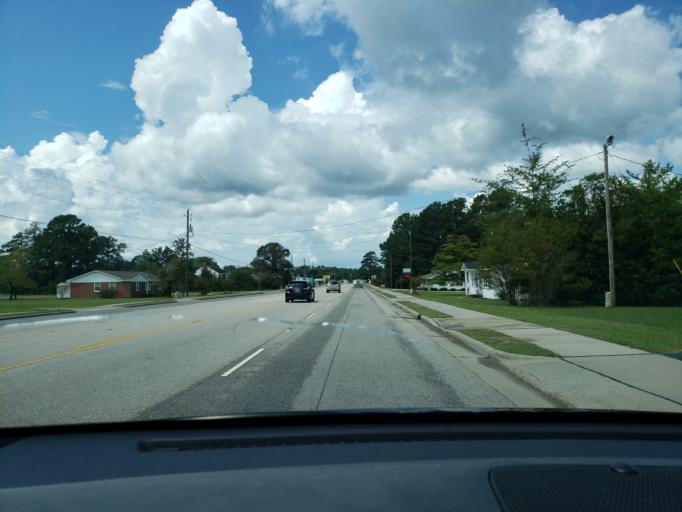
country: US
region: North Carolina
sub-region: Bladen County
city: Elizabethtown
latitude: 34.6551
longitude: -78.7204
